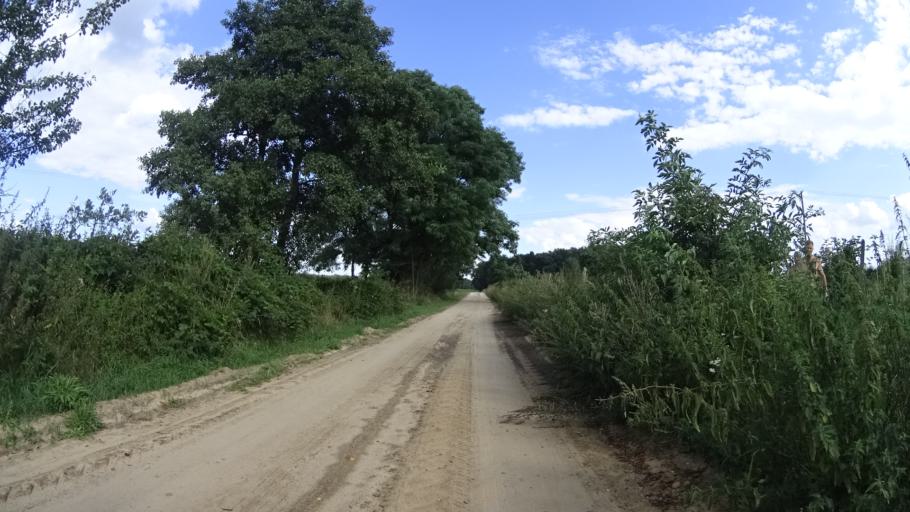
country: PL
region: Masovian Voivodeship
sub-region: Powiat grojecki
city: Mogielnica
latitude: 51.6778
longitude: 20.7688
